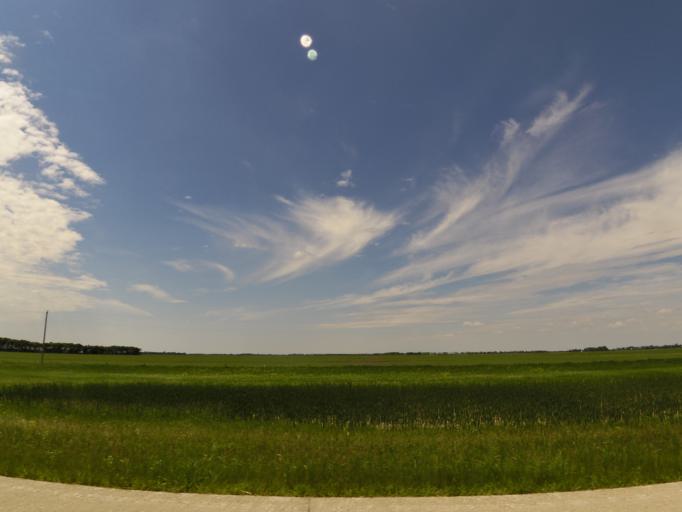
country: US
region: North Dakota
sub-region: Walsh County
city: Grafton
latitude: 48.3308
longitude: -97.1897
